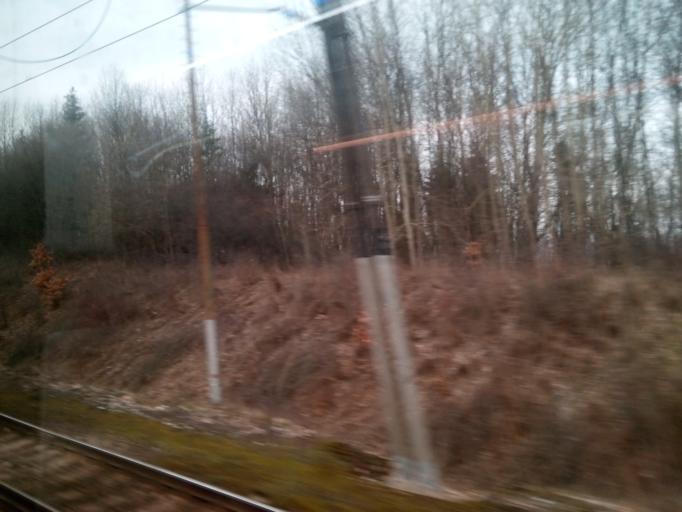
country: SK
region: Zilinsky
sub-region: Okres Liptovsky Mikulas
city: Liptovsky Mikulas
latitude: 49.0908
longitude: 19.5136
